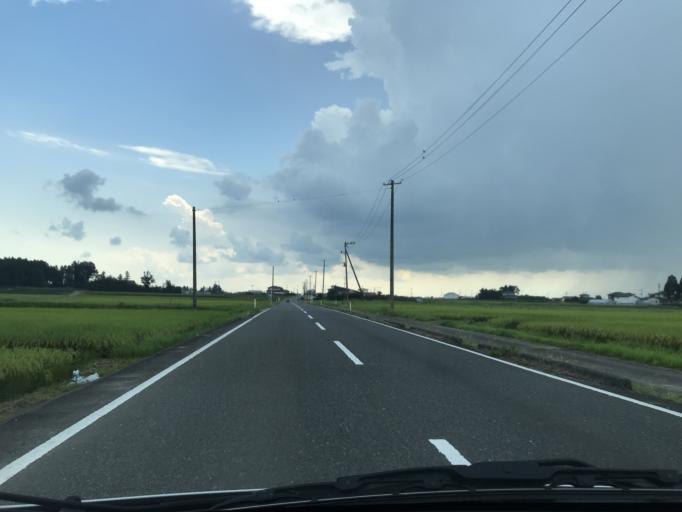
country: JP
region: Iwate
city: Ichinoseki
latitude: 38.7657
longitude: 141.0698
